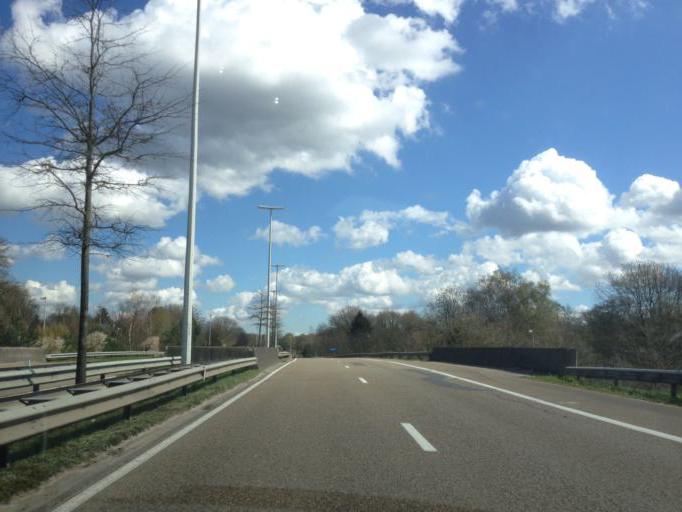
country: BE
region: Flanders
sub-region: Provincie Limburg
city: Genk
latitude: 50.9683
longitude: 5.5316
